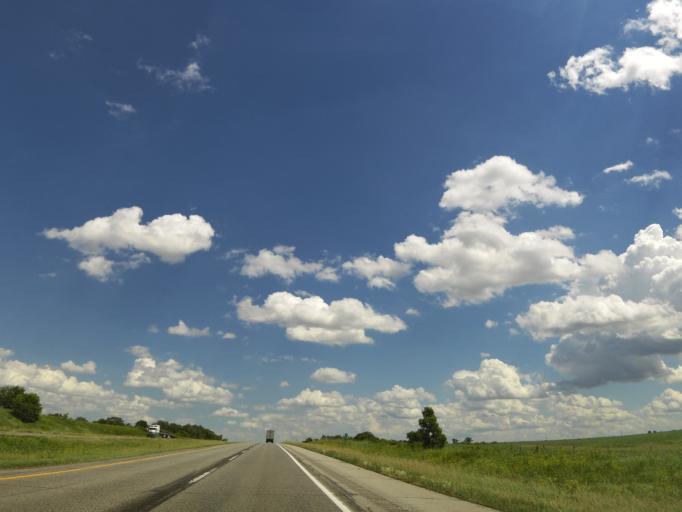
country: US
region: Iowa
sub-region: Linn County
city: Center Point
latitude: 42.1892
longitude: -91.8079
